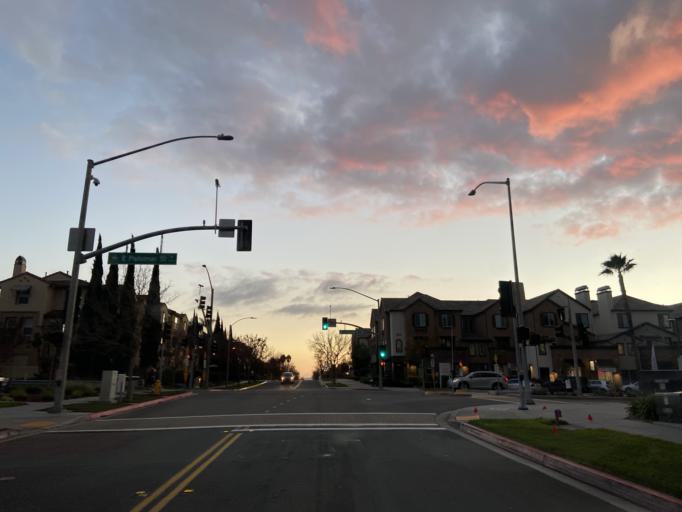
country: US
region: California
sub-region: San Diego County
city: Bonita
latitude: 32.6270
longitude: -116.9747
